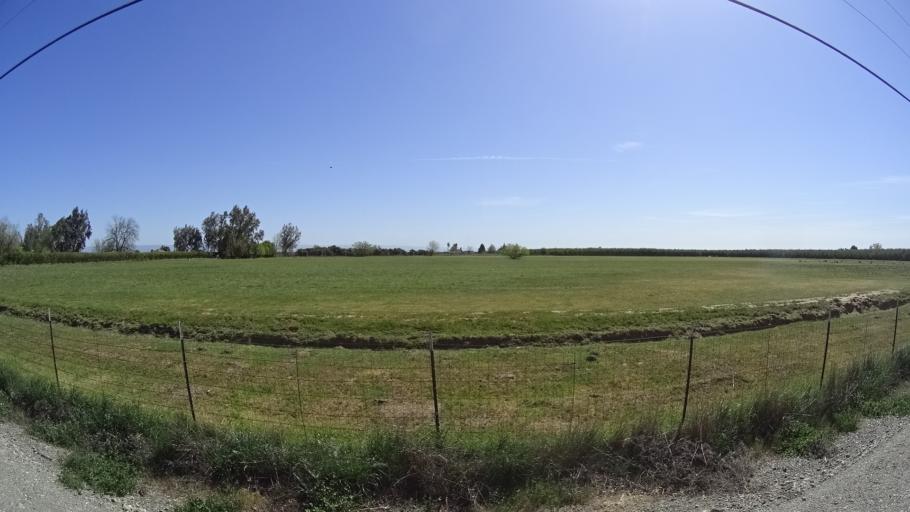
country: US
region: California
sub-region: Glenn County
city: Hamilton City
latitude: 39.7257
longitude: -122.1044
